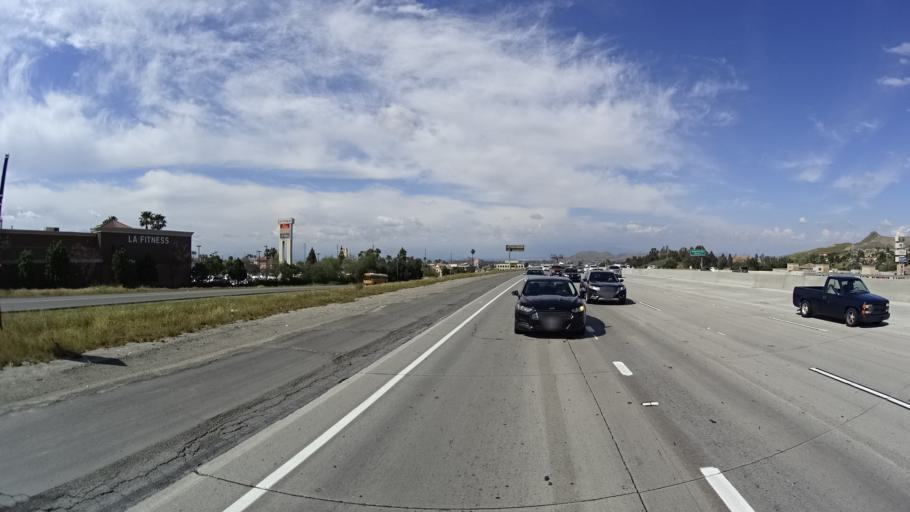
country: US
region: California
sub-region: Riverside County
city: El Cerrito
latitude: 33.8428
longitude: -117.5351
